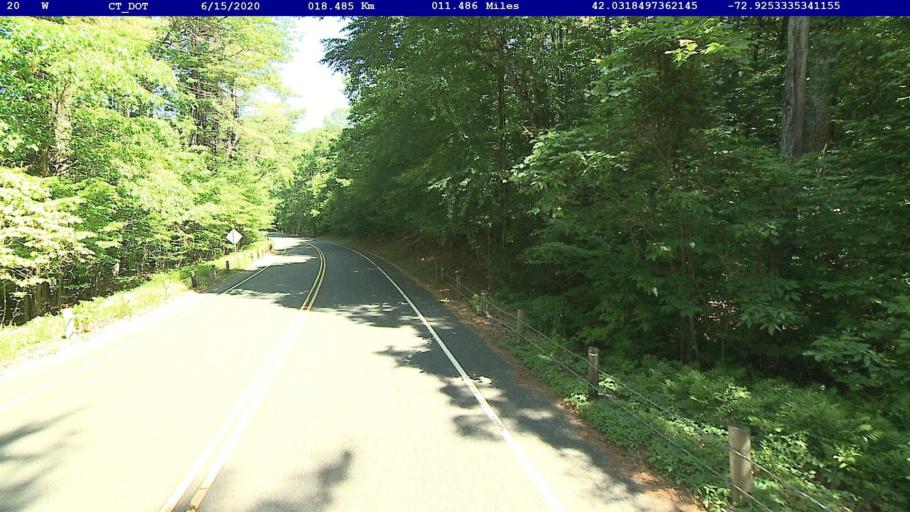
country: US
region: Massachusetts
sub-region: Hampden County
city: Granville
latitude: 42.0319
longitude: -72.9254
